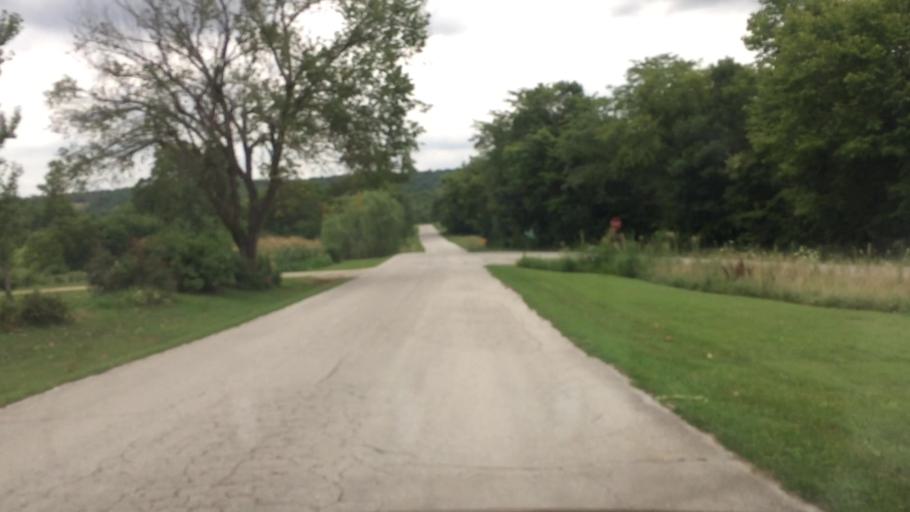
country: US
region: Missouri
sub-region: Greene County
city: Strafford
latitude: 37.3232
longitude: -93.0574
